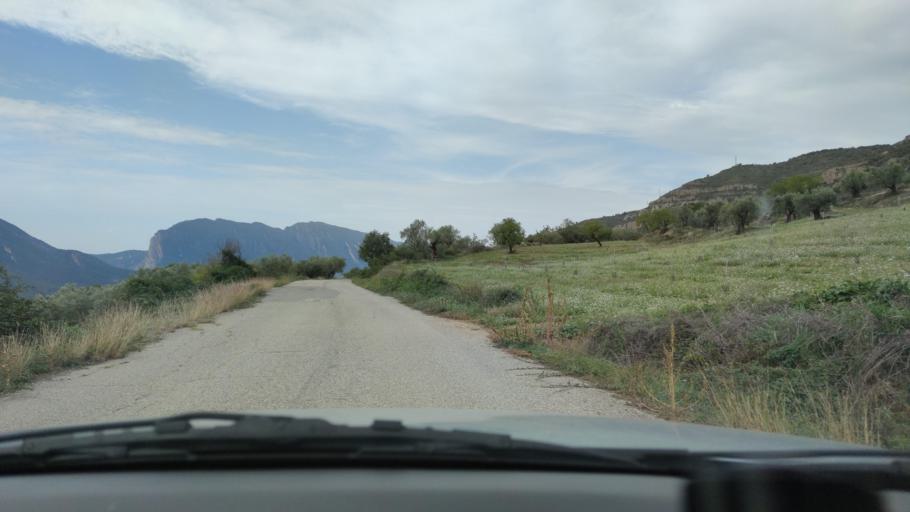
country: ES
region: Catalonia
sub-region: Provincia de Lleida
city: Llimiana
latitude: 42.0684
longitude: 0.9516
